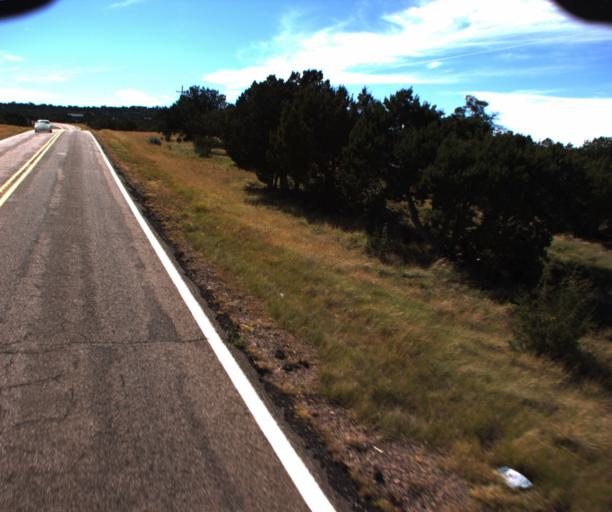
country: US
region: Arizona
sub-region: Navajo County
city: White Mountain Lake
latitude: 34.3196
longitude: -109.7623
